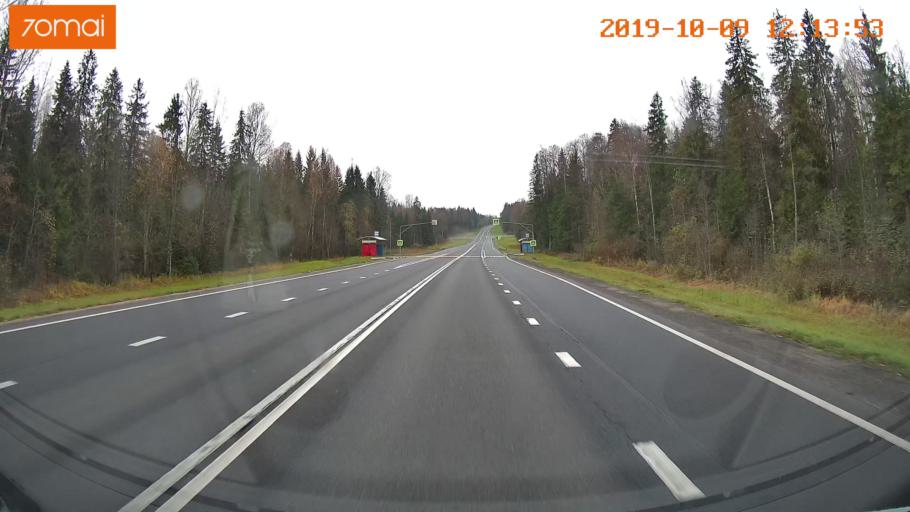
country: RU
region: Jaroslavl
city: Prechistoye
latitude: 58.5037
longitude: 40.3430
